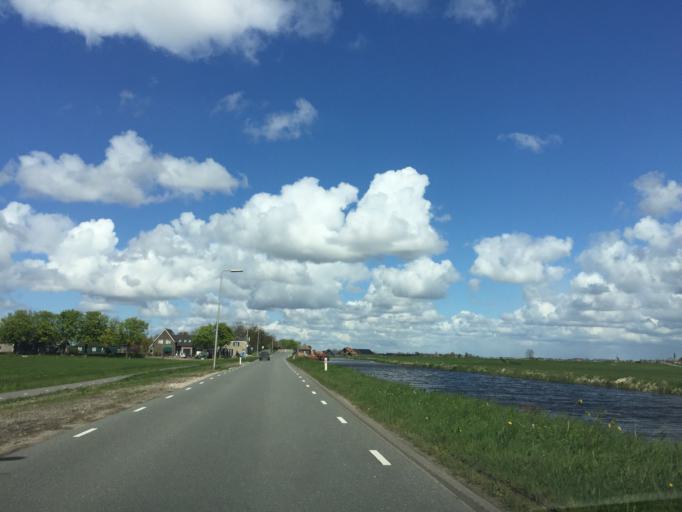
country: NL
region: South Holland
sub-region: Gemeente Leiderdorp
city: Leiderdorp
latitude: 52.1819
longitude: 4.5396
